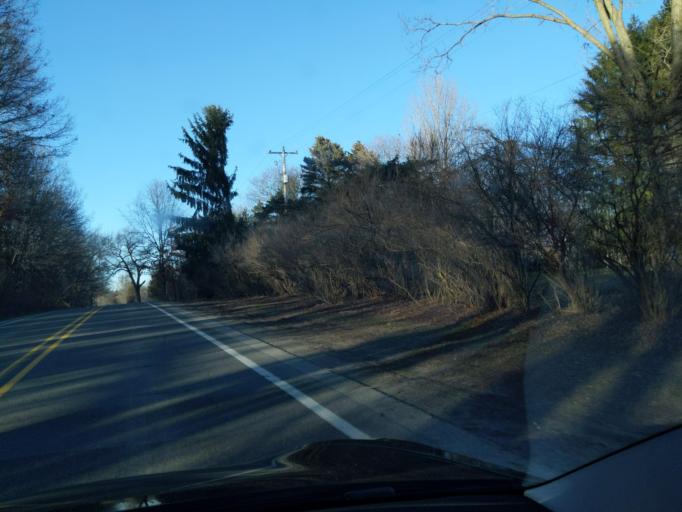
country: US
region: Michigan
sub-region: Washtenaw County
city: Chelsea
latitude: 42.3399
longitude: -84.0271
